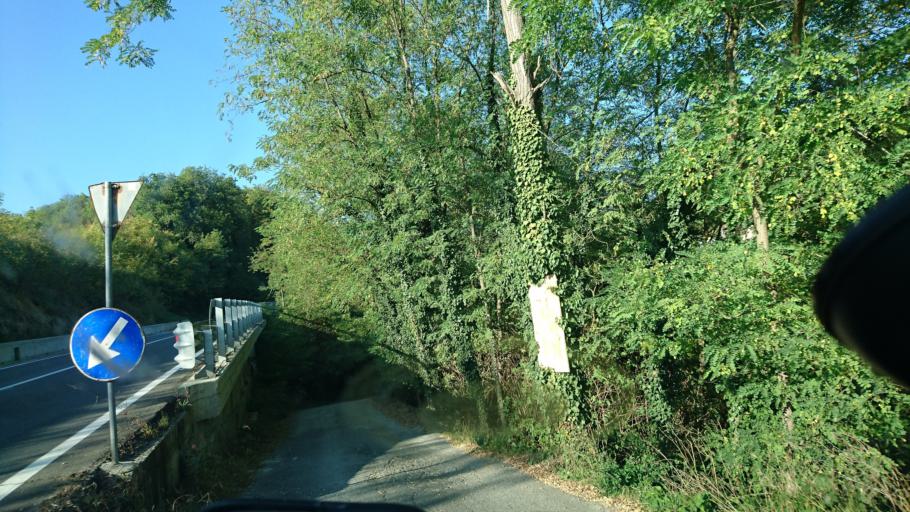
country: IT
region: Piedmont
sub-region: Provincia di Asti
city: Bubbio
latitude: 44.6688
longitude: 8.3028
